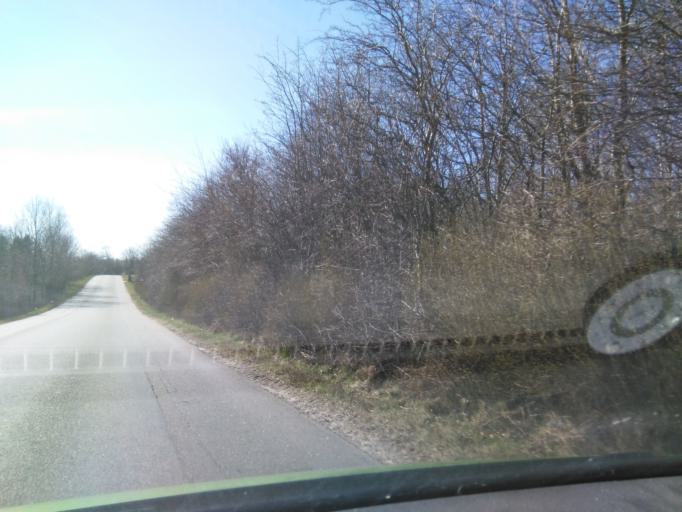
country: DK
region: Central Jutland
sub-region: Favrskov Kommune
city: Soften
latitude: 56.2442
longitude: 10.1125
